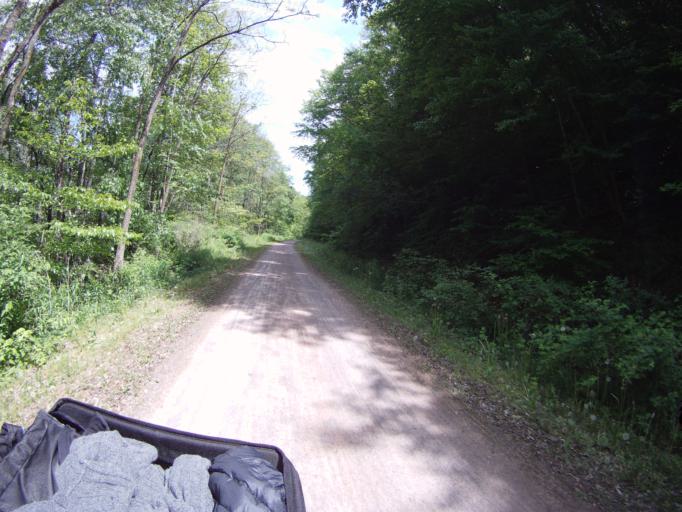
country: US
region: Pennsylvania
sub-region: Somerset County
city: Meyersdale
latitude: 39.8074
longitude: -78.9884
